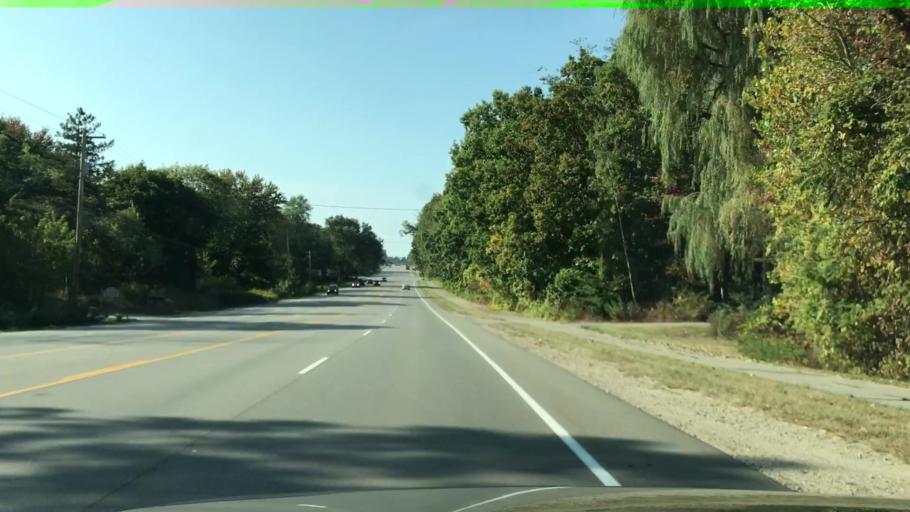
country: US
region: Michigan
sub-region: Kent County
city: Forest Hills
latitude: 42.9329
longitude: -85.5245
